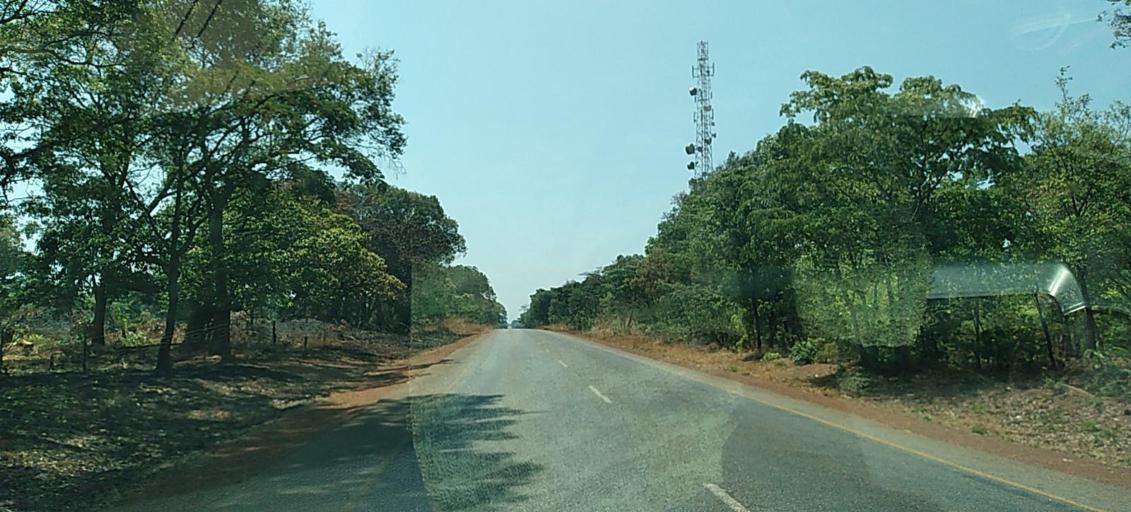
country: ZM
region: North-Western
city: Solwezi
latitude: -12.3671
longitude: 25.9843
